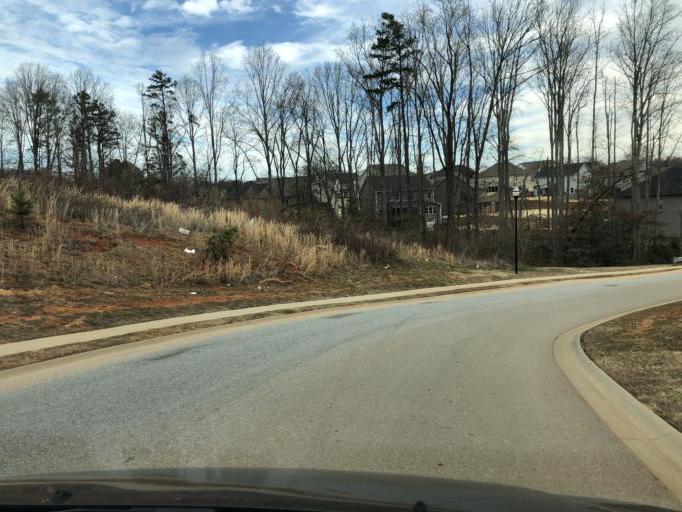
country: US
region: South Carolina
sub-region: Greenville County
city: Five Forks
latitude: 34.8497
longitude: -82.1997
